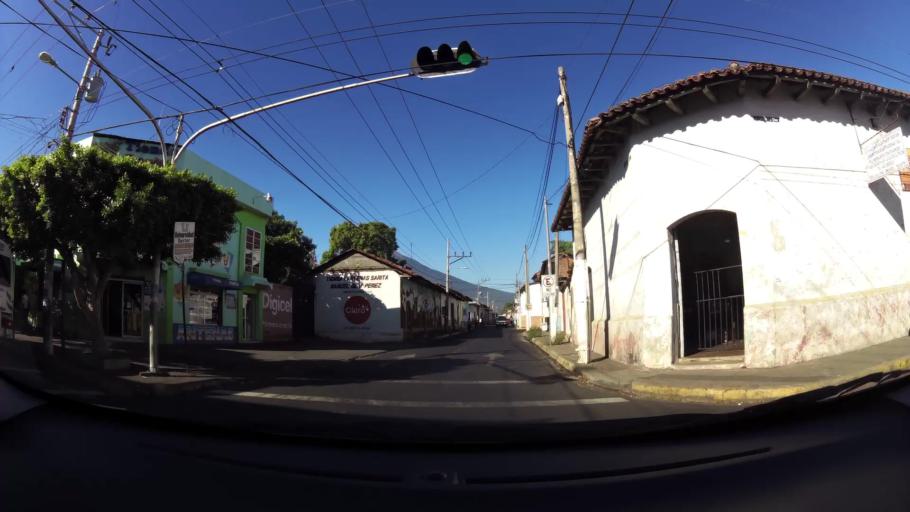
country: SV
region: San Miguel
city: San Miguel
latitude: 13.4778
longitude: -88.1740
